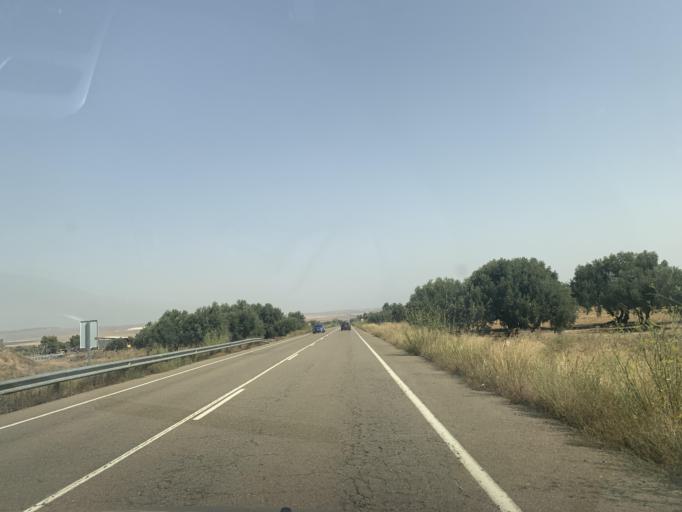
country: ES
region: Aragon
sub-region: Provincia de Zaragoza
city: Belchite
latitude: 41.3126
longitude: -0.7422
